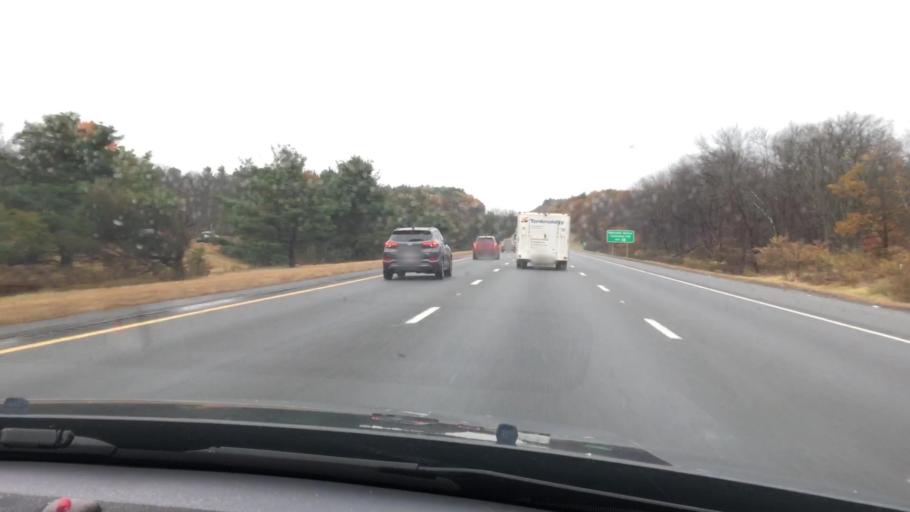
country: US
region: Massachusetts
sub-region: Middlesex County
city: Westford
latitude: 42.5809
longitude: -71.4028
